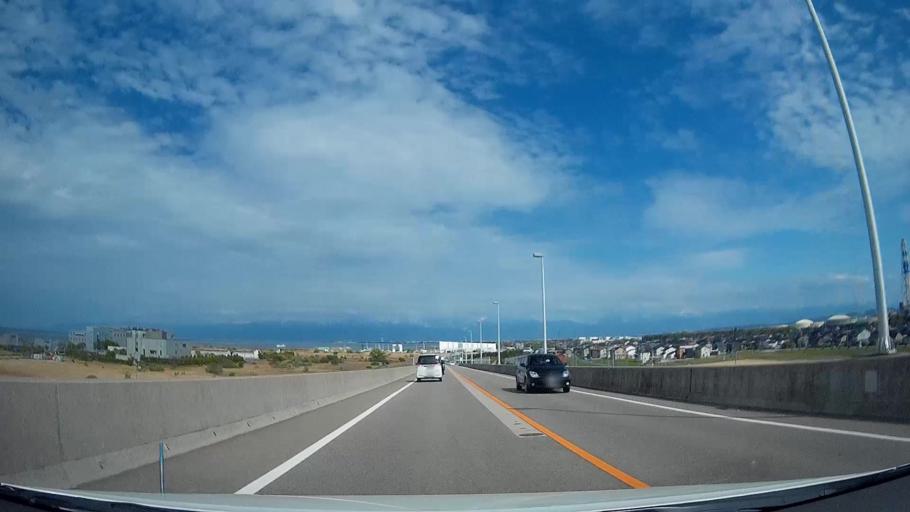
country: JP
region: Toyama
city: Kuragaki-kosugi
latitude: 36.7746
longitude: 137.1261
